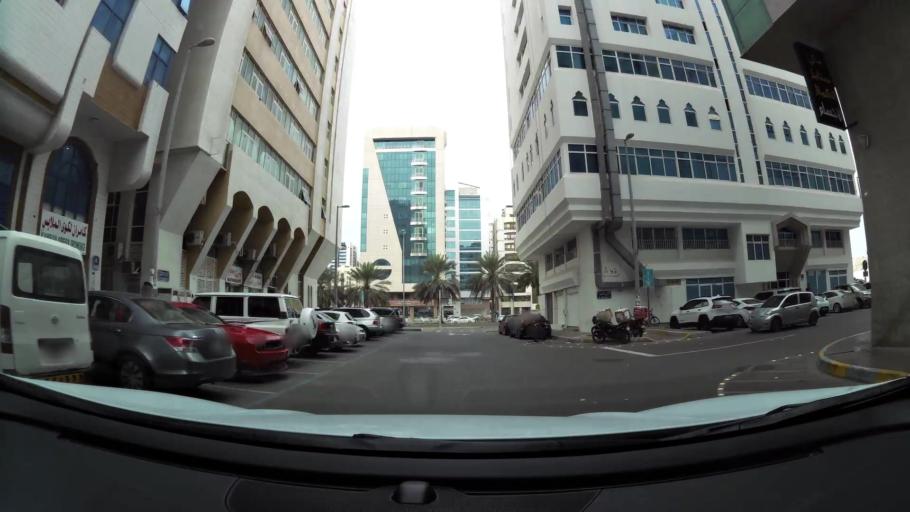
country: AE
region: Abu Dhabi
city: Abu Dhabi
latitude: 24.4910
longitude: 54.3828
